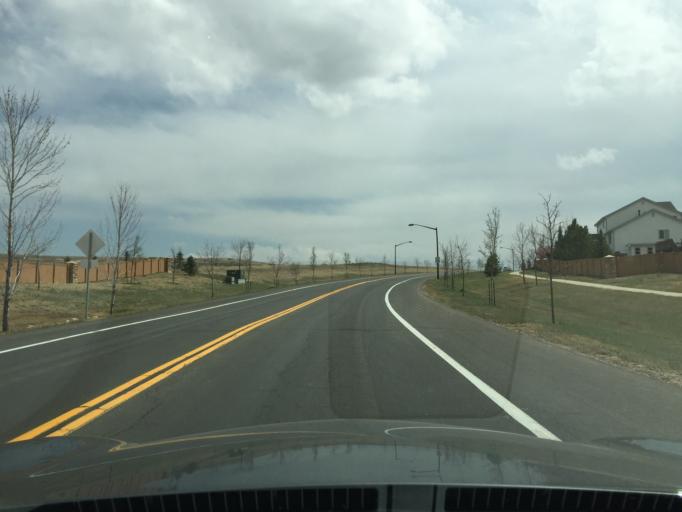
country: US
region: Colorado
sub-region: Boulder County
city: Erie
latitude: 40.0203
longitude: -105.0386
